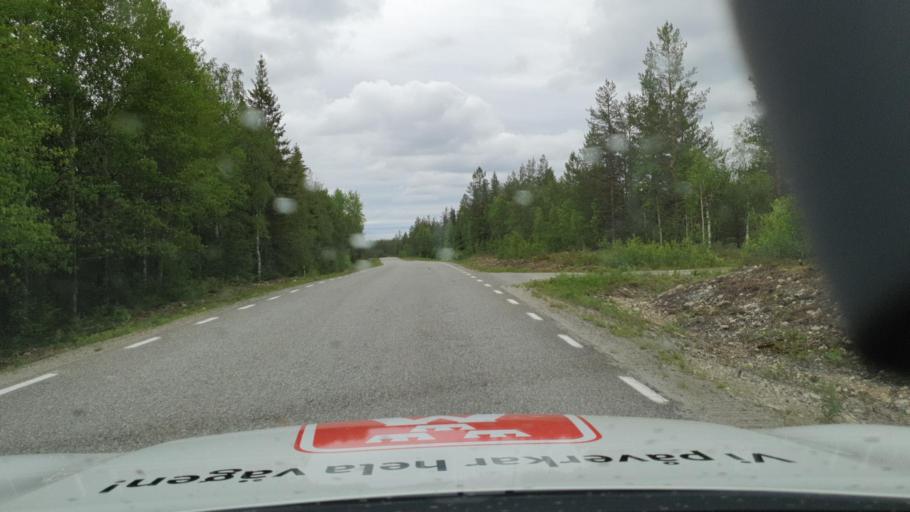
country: SE
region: Vaesterbotten
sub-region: Lycksele Kommun
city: Lycksele
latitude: 64.2237
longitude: 18.2493
